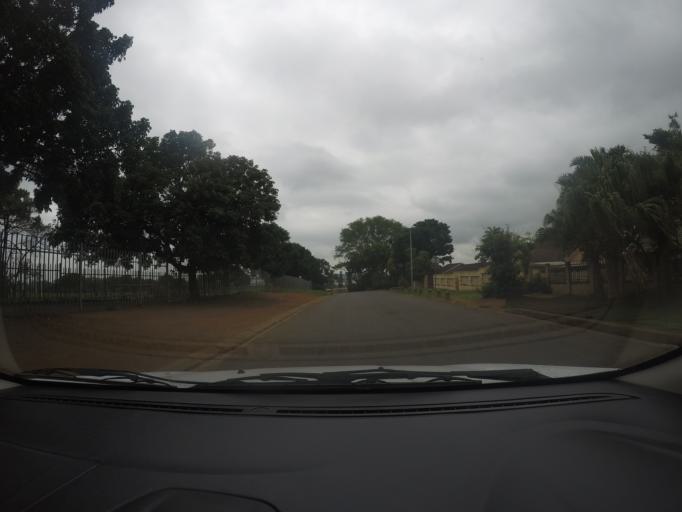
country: ZA
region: KwaZulu-Natal
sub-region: uThungulu District Municipality
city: Empangeni
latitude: -28.7678
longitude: 31.8961
